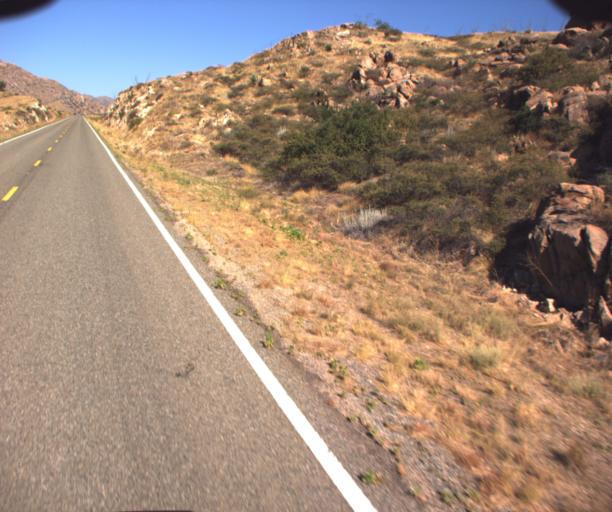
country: US
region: Arizona
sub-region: Graham County
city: Swift Trail Junction
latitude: 32.5603
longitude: -109.7617
